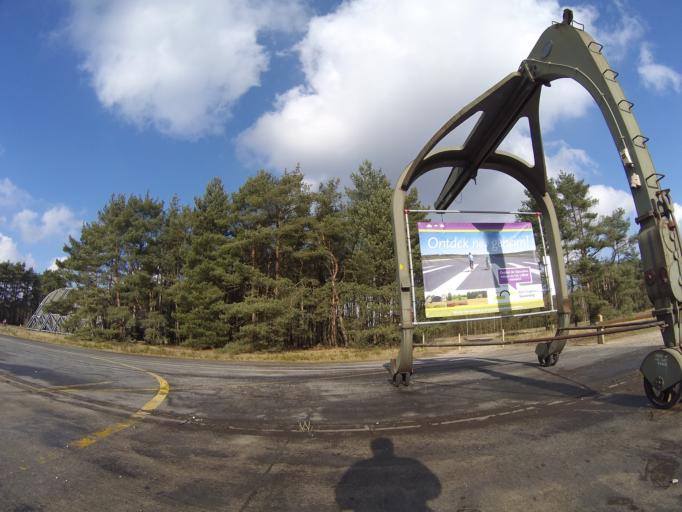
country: NL
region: Utrecht
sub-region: Gemeente Zeist
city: Zeist
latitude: 52.1300
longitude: 5.2616
